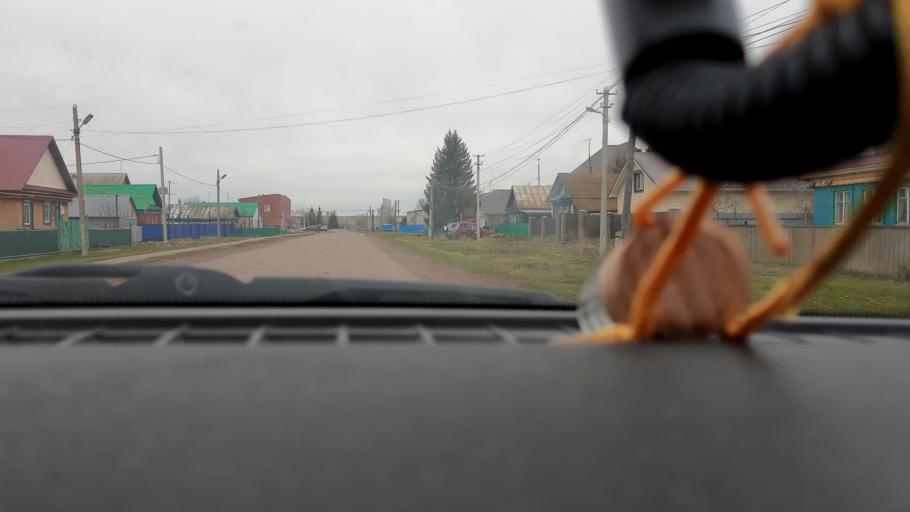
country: RU
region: Bashkortostan
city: Asanovo
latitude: 54.8135
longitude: 55.5690
